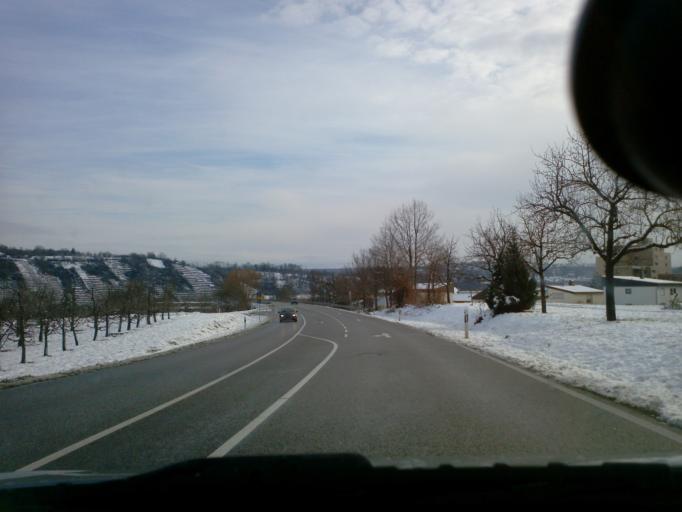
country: DE
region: Baden-Wuerttemberg
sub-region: Regierungsbezirk Stuttgart
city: Walheim
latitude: 49.0184
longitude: 9.1522
